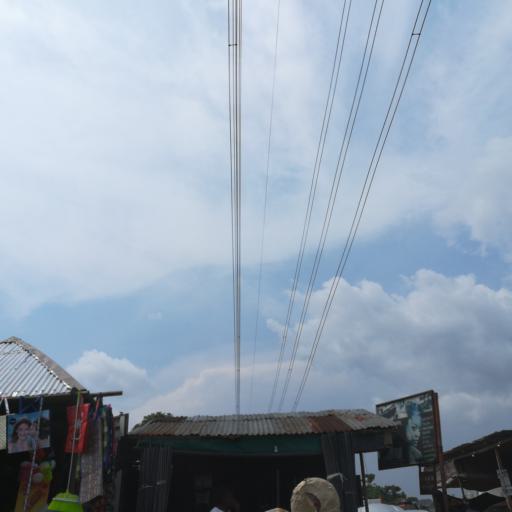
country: NG
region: Rivers
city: Port Harcourt
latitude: 4.8612
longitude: 7.0215
